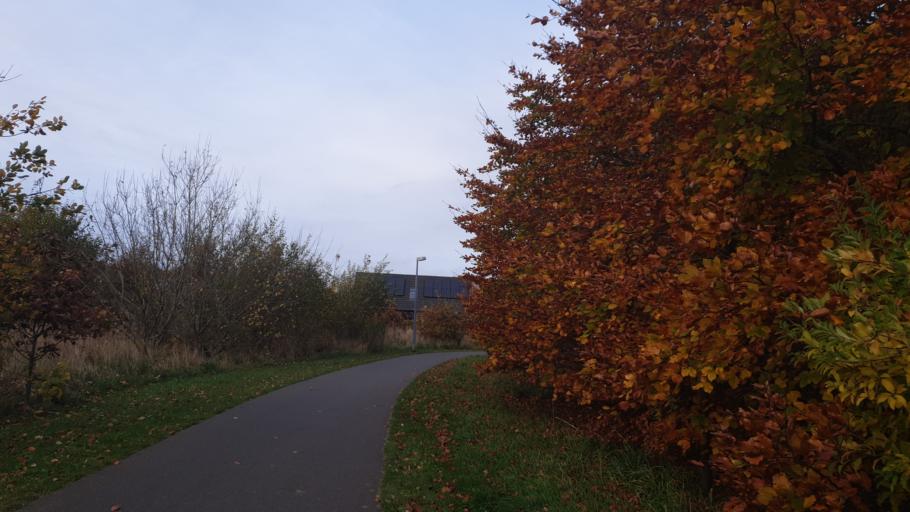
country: DK
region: Central Jutland
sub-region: Hedensted Kommune
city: Hedensted
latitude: 55.7901
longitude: 9.6923
